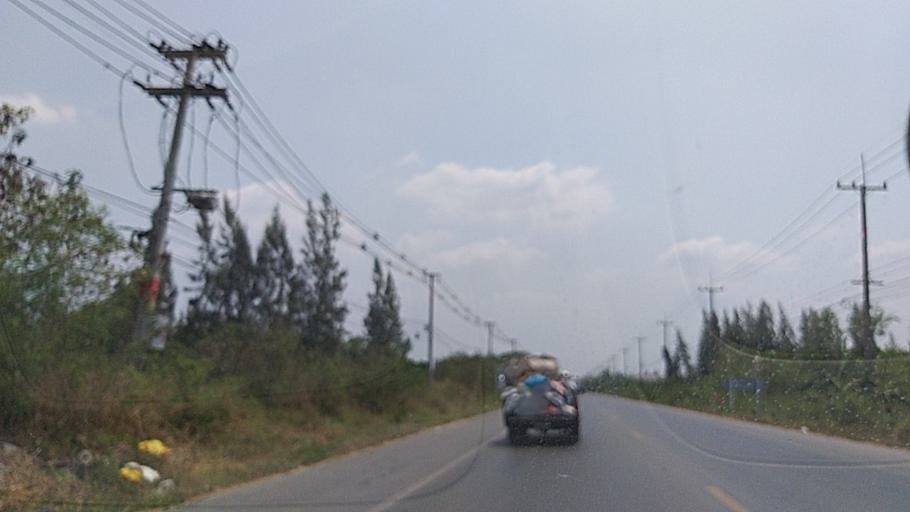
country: TH
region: Chachoengsao
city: Chachoengsao
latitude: 13.7675
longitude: 101.0689
